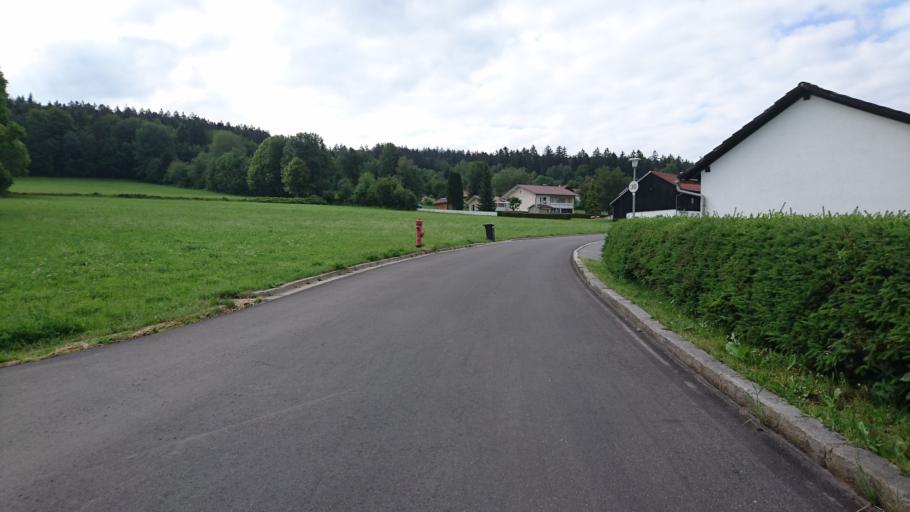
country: DE
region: Bavaria
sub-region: Lower Bavaria
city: Neuschonau
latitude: 48.8819
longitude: 13.4790
